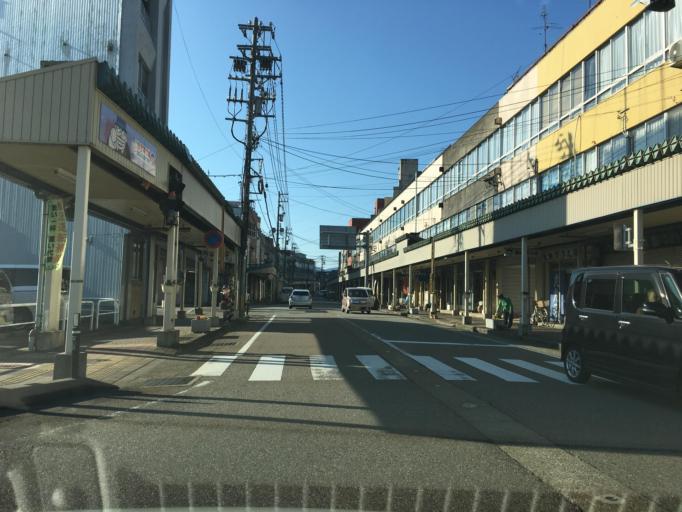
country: JP
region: Toyama
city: Himi
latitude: 36.8595
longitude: 136.9868
